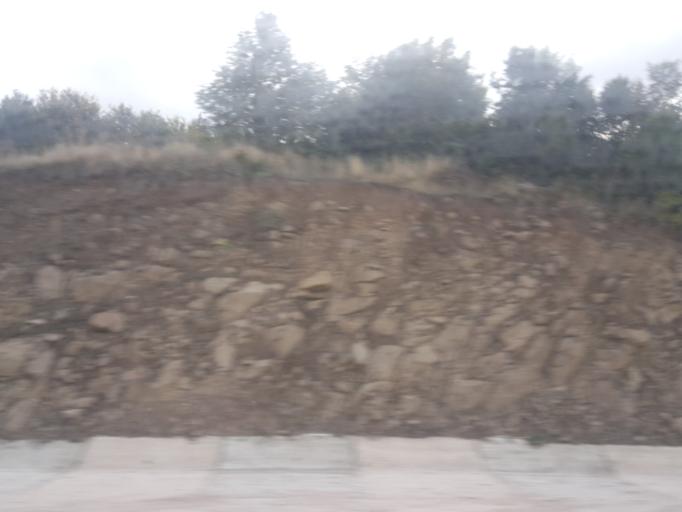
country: TR
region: Tokat
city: Bereketli
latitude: 40.5522
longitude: 37.3004
